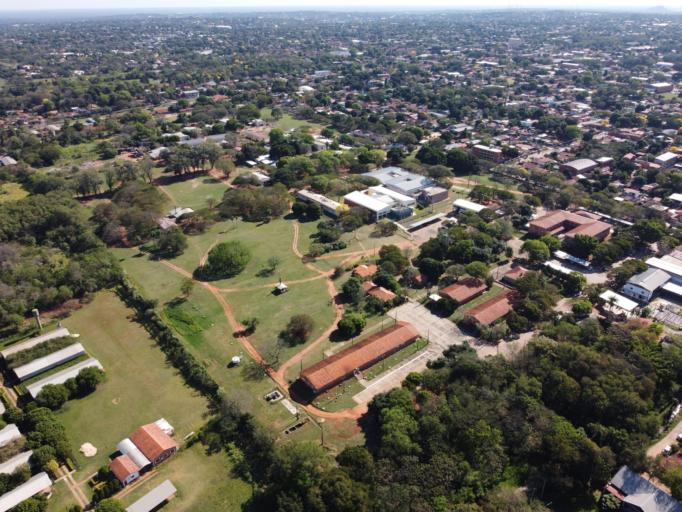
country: PY
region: Central
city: Fernando de la Mora
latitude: -25.3393
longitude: -57.5261
